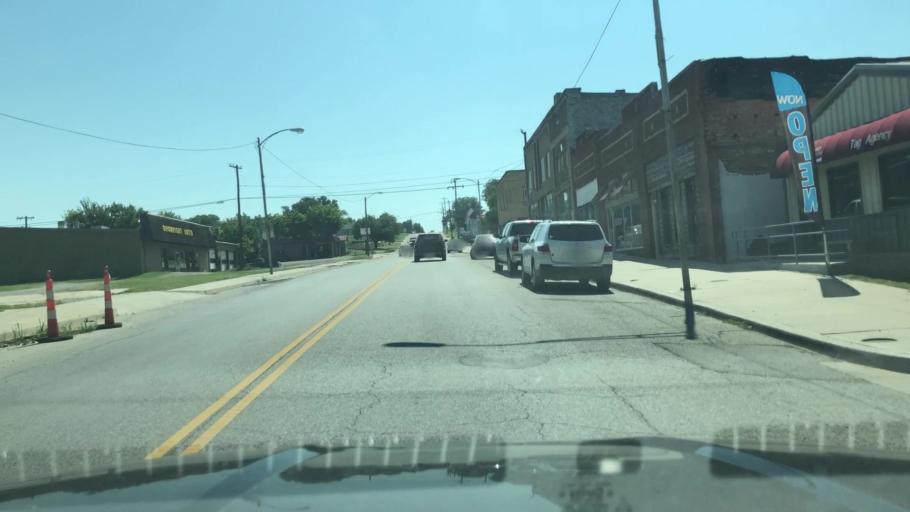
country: US
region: Oklahoma
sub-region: Creek County
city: Drumright
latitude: 35.9885
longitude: -96.5968
